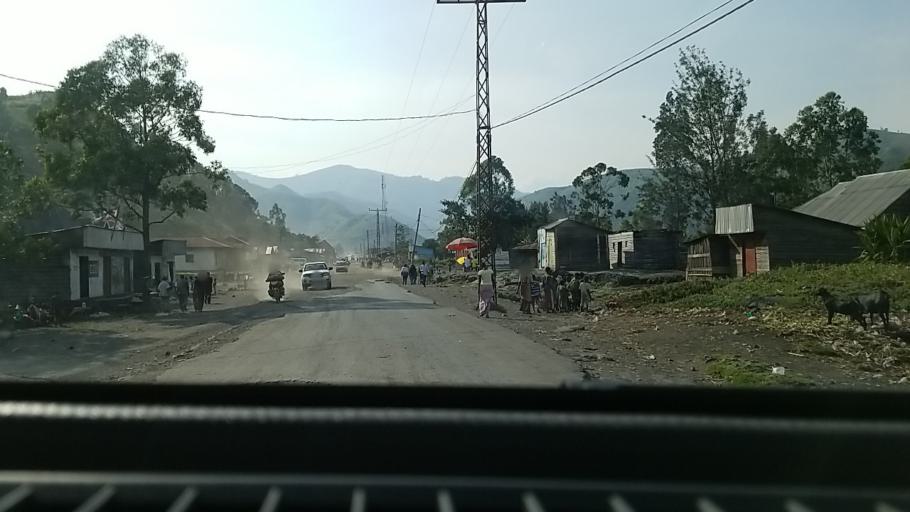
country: CD
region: Nord Kivu
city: Sake
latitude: -1.5723
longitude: 29.0583
